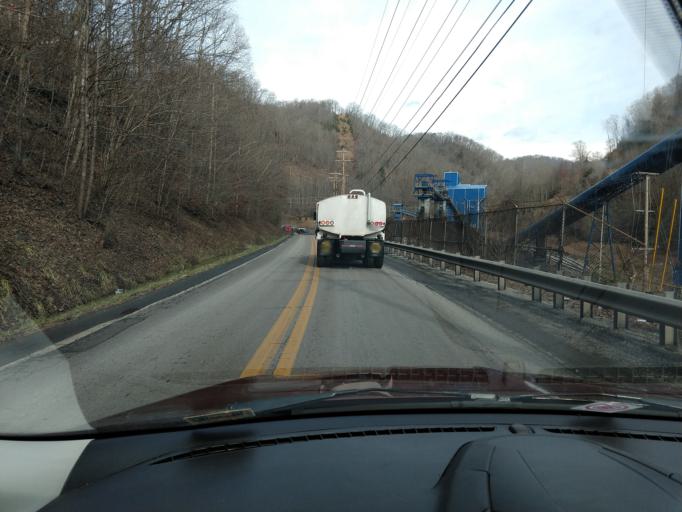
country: US
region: West Virginia
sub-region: McDowell County
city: Welch
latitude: 37.3308
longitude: -81.6854
